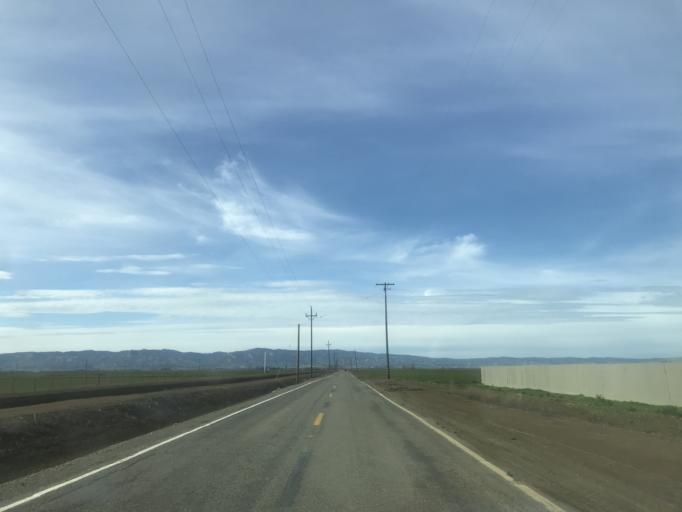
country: US
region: California
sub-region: Yolo County
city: Cottonwood
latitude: 38.6637
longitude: -121.9092
